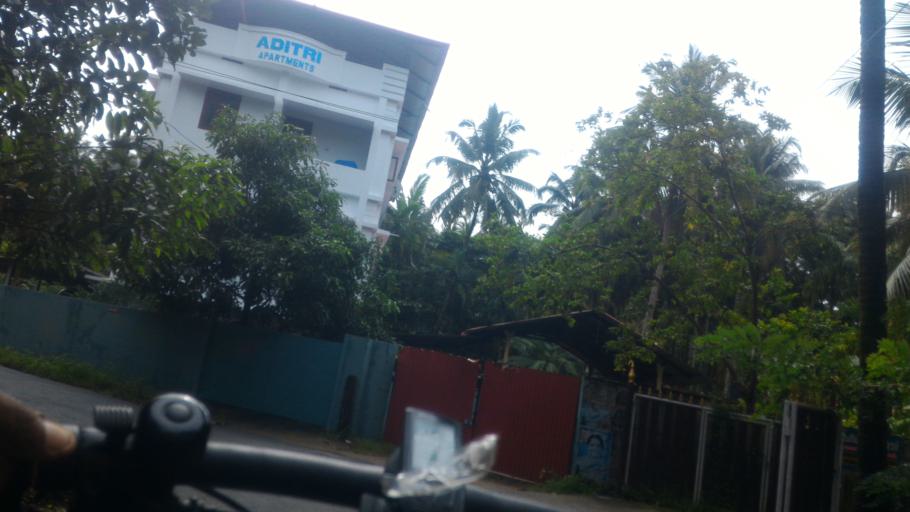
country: IN
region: Kerala
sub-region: Thrissur District
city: Thanniyam
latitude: 10.4226
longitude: 76.1104
